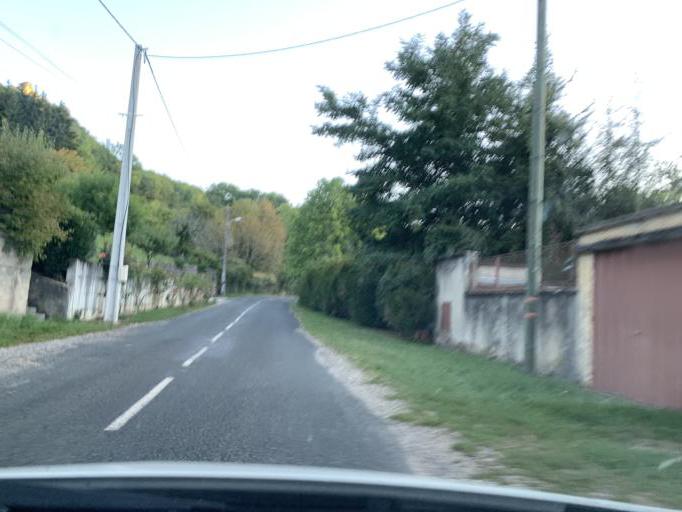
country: FR
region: Rhone-Alpes
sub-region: Departement de l'Ain
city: Saint-Rambert-en-Bugey
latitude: 45.9246
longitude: 5.4018
